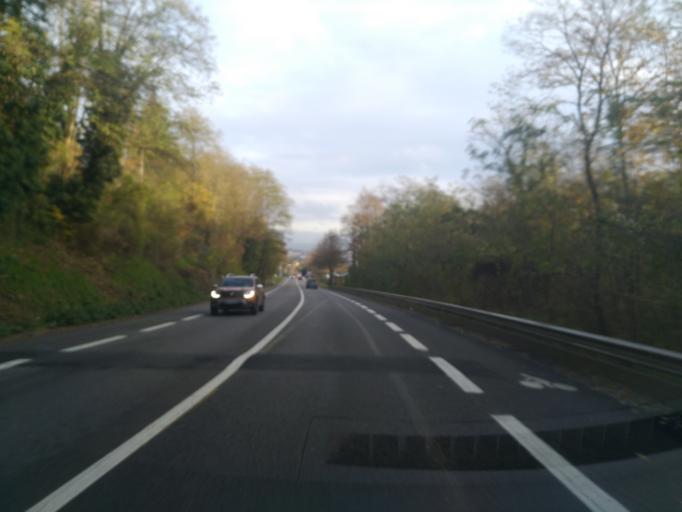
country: FR
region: Ile-de-France
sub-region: Departement des Yvelines
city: Fourqueux
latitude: 48.8800
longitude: 2.0644
